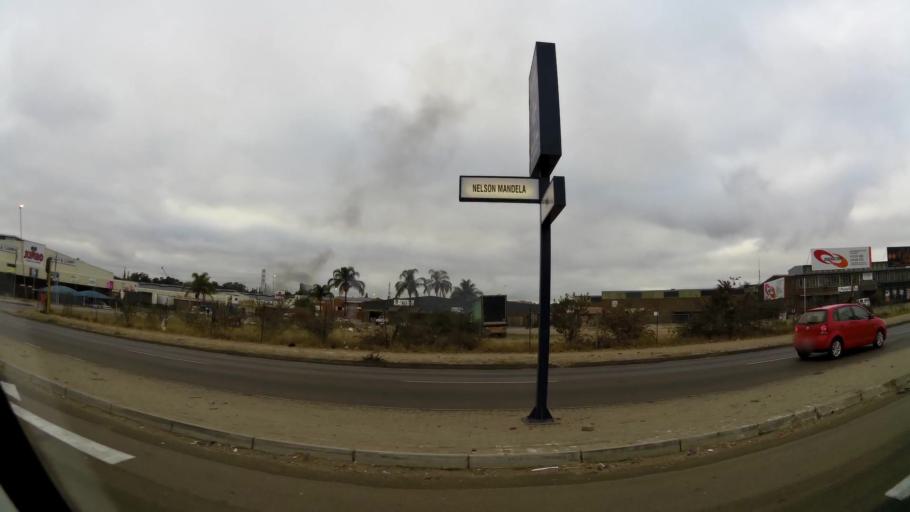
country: ZA
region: Limpopo
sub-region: Capricorn District Municipality
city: Polokwane
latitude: -23.9093
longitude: 29.4406
